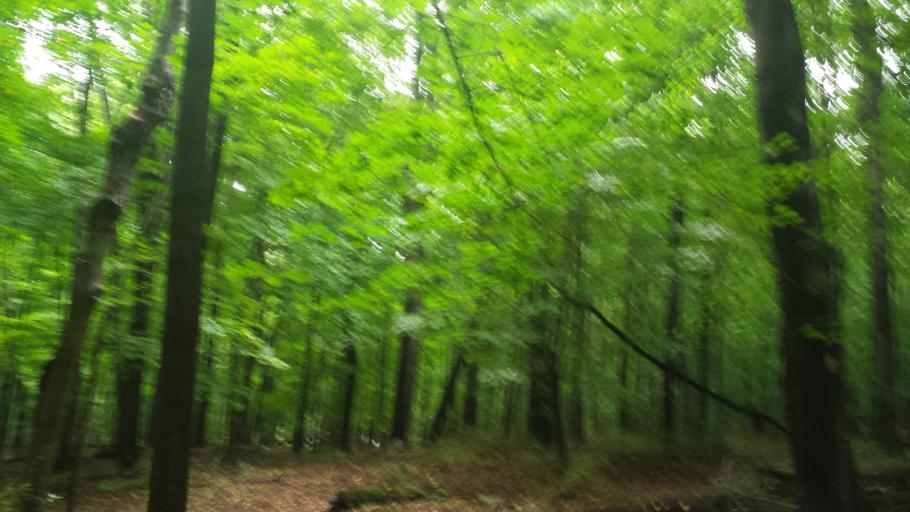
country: US
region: New York
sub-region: Westchester County
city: Hawthorne
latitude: 41.1194
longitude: -73.8000
